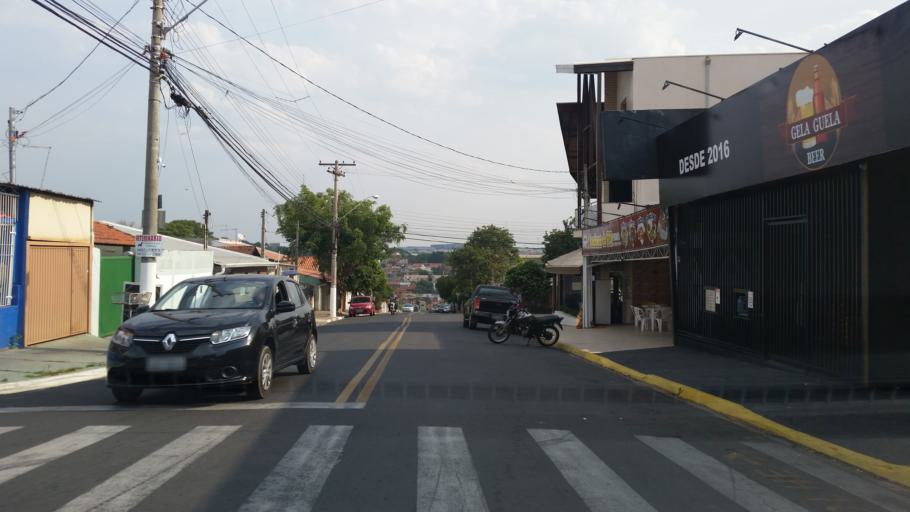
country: BR
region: Sao Paulo
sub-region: Hortolandia
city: Hortolandia
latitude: -22.8825
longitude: -47.1766
